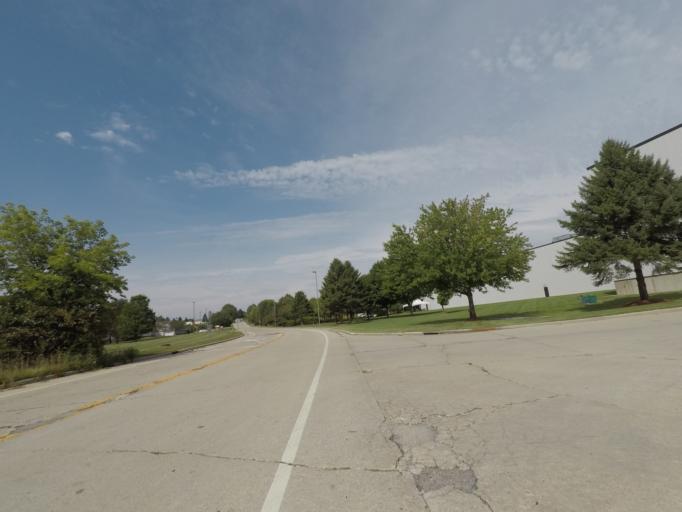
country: US
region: Wisconsin
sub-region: Jefferson County
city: Fort Atkinson
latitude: 42.9426
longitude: -88.8333
